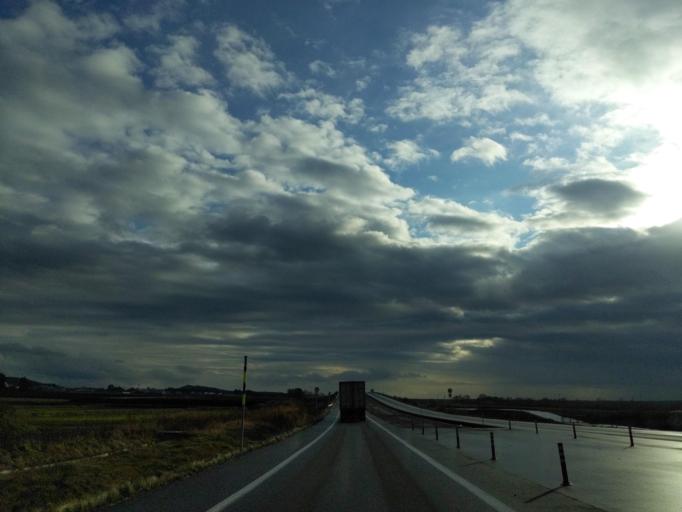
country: JP
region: Hokkaido
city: Chitose
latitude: 42.9334
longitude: 141.7148
